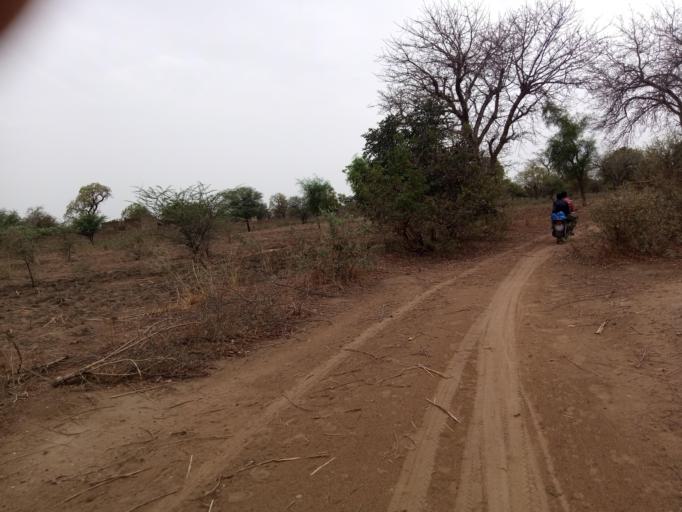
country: BF
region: Boucle du Mouhoun
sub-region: Province de la Kossi
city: Nouna
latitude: 12.7560
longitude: -3.9910
